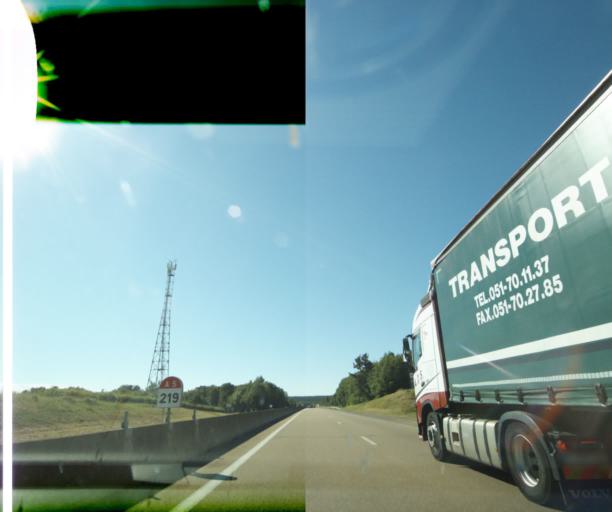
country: FR
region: Champagne-Ardenne
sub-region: Departement de la Haute-Marne
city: Chamarandes-Choignes
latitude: 47.9650
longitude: 5.1466
